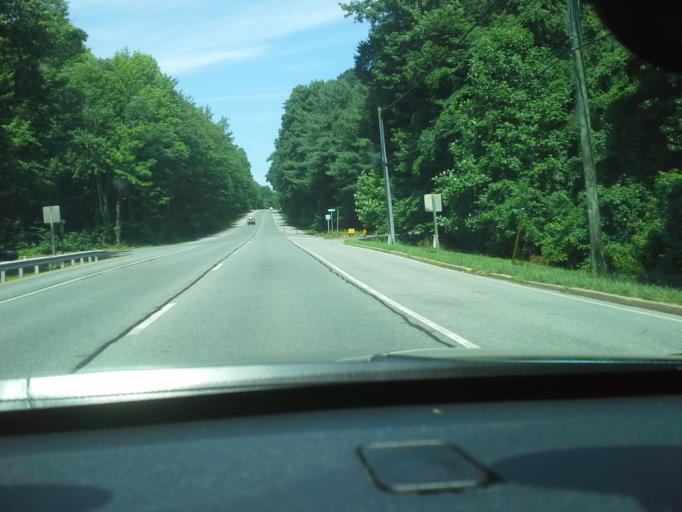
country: US
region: Maryland
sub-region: Calvert County
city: Chesapeake Beach
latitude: 38.7001
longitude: -76.5558
